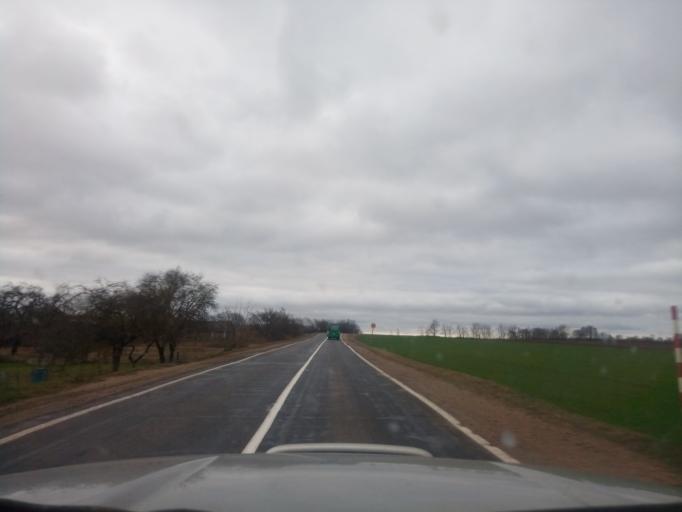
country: BY
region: Minsk
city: Kapyl'
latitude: 53.1742
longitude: 27.1625
